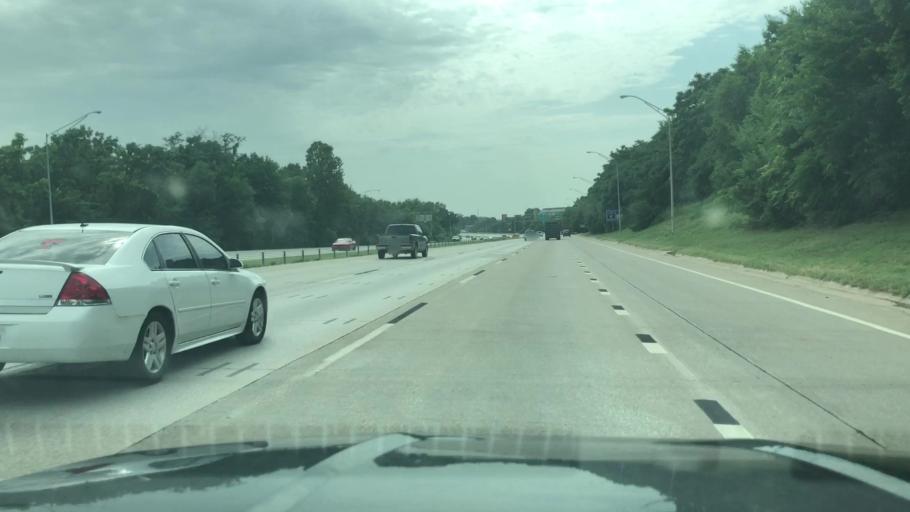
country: US
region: Oklahoma
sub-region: Tulsa County
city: Tulsa
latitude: 36.1560
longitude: -96.0123
